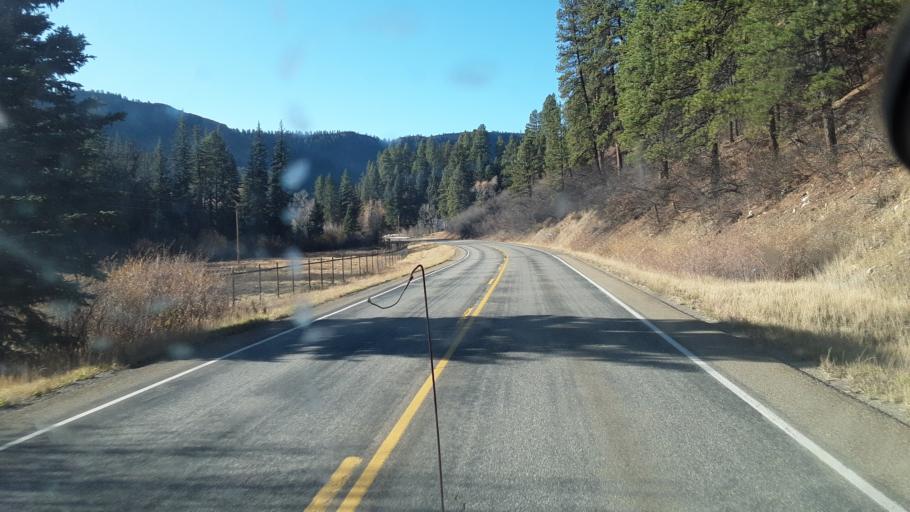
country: US
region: Colorado
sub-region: La Plata County
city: Durango
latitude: 37.3385
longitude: -107.7237
